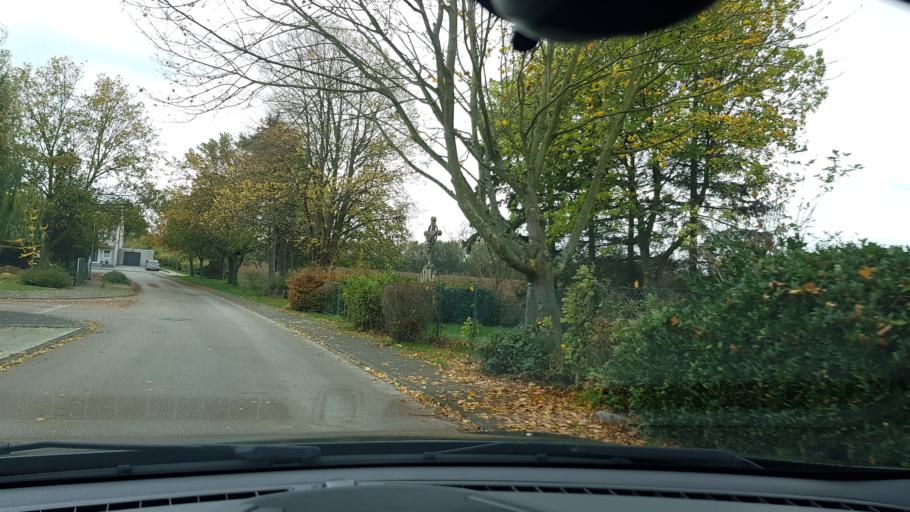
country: DE
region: North Rhine-Westphalia
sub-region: Regierungsbezirk Koln
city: Bedburg
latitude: 51.0014
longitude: 6.5414
